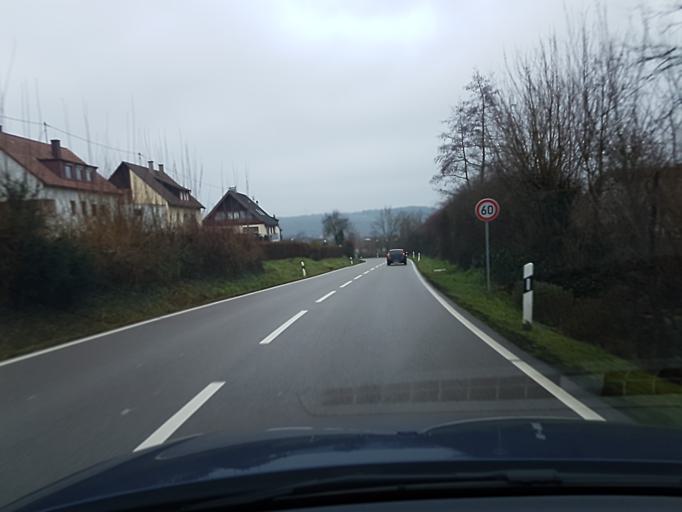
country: DE
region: Baden-Wuerttemberg
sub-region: Regierungsbezirk Stuttgart
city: Besigheim
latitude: 48.9928
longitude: 9.1527
